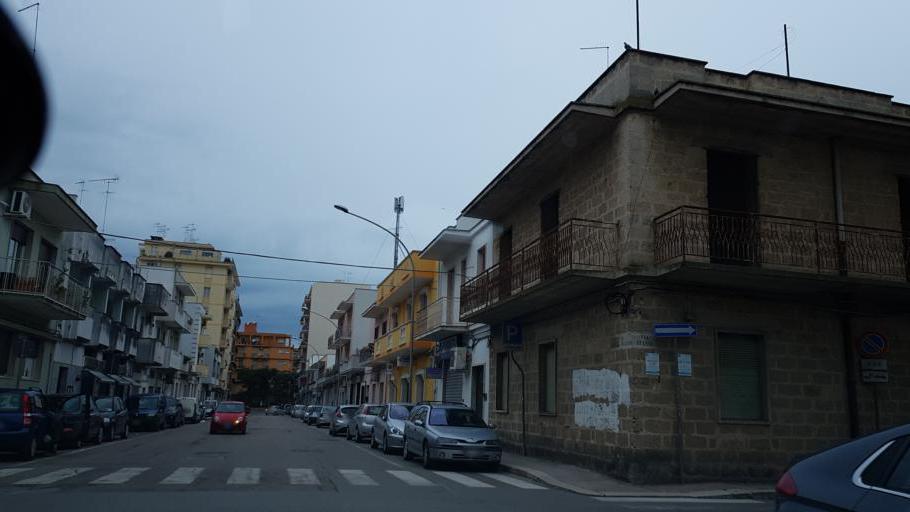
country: IT
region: Apulia
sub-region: Provincia di Brindisi
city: Brindisi
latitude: 40.6305
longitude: 17.9250
